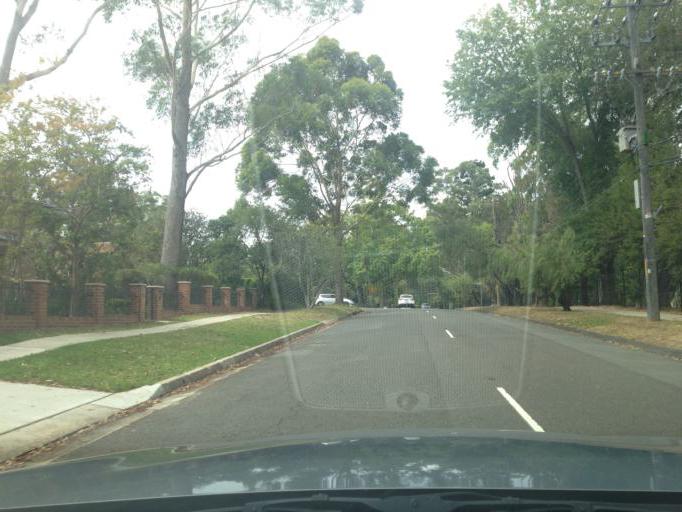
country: AU
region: New South Wales
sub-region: Ku-ring-gai
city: Killara
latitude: -33.7741
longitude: 151.1509
